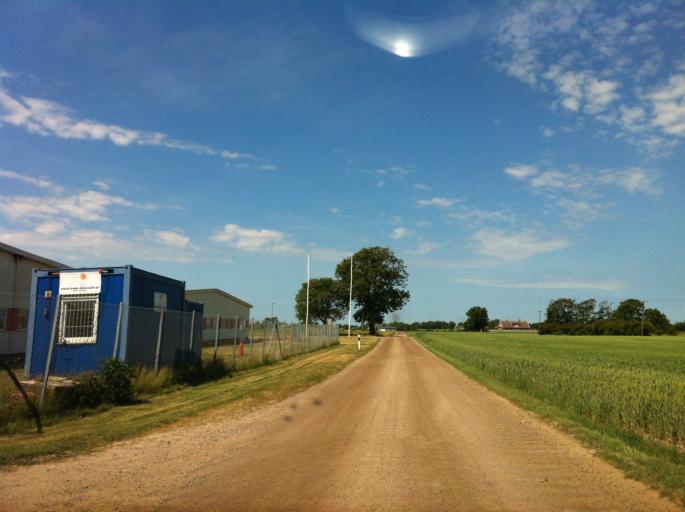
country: SE
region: Skane
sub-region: Landskrona
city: Asmundtorp
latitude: 55.9398
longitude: 12.8907
